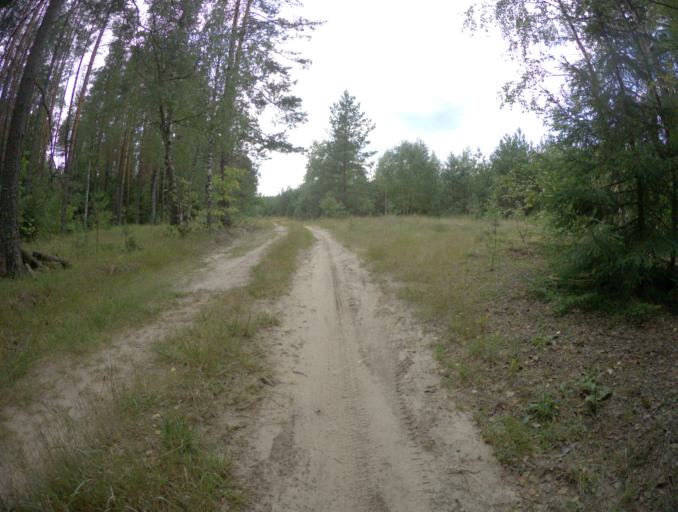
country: RU
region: Vladimir
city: Vorsha
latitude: 55.9648
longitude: 40.1610
